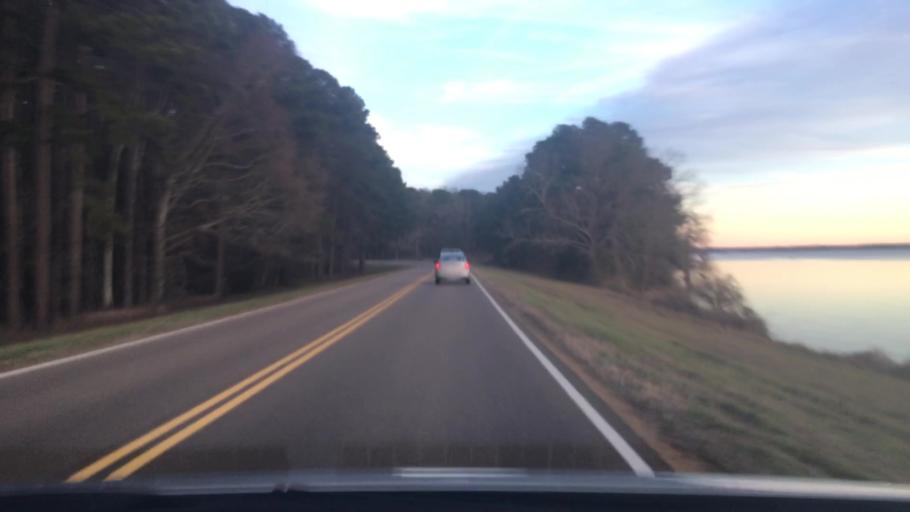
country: US
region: Mississippi
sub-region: Madison County
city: Canton
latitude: 32.5165
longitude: -89.9867
